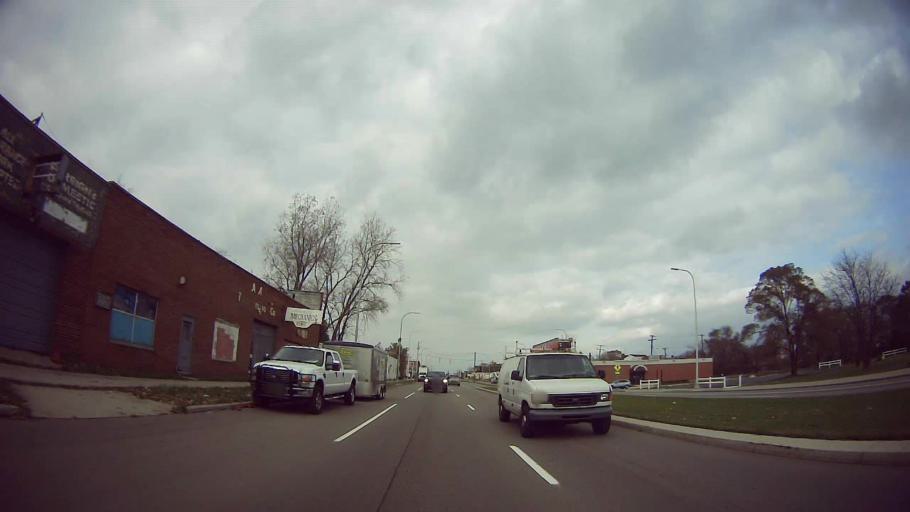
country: US
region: Michigan
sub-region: Wayne County
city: Highland Park
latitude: 42.3777
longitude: -83.1393
